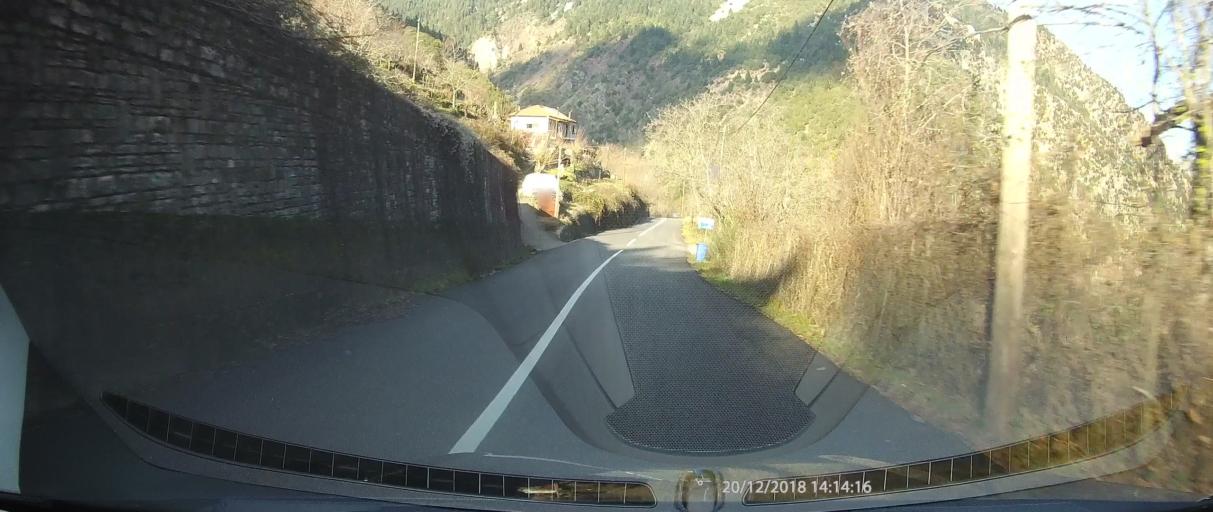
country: GR
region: West Greece
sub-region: Nomos Aitolias kai Akarnanias
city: Thermo
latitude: 38.7464
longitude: 21.6528
